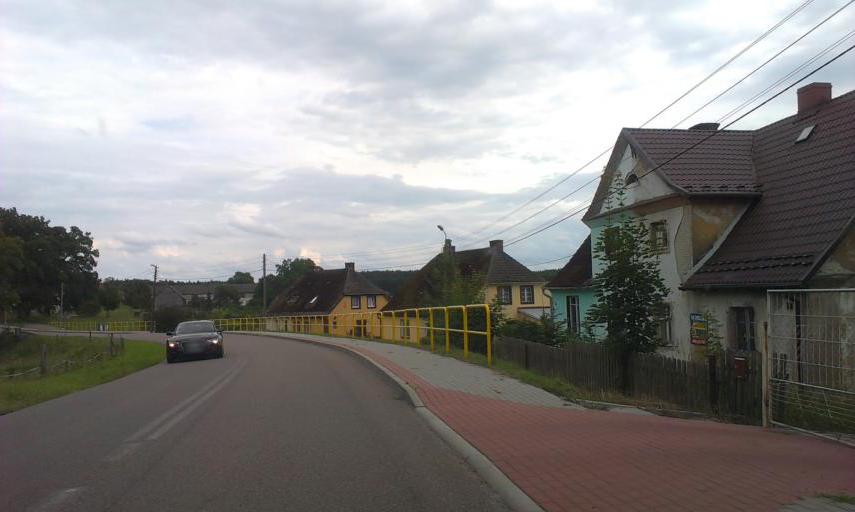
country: PL
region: West Pomeranian Voivodeship
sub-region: Powiat szczecinecki
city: Barwice
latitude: 53.7582
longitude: 16.2443
